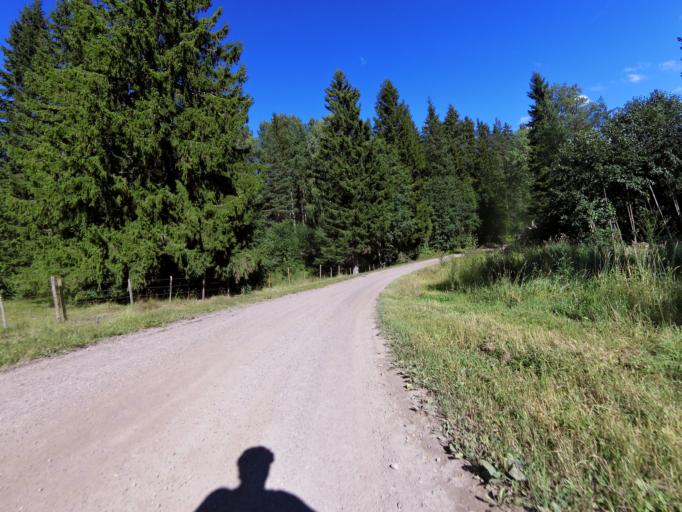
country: SE
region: Gaevleborg
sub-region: Hofors Kommun
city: Hofors
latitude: 60.5308
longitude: 16.4110
